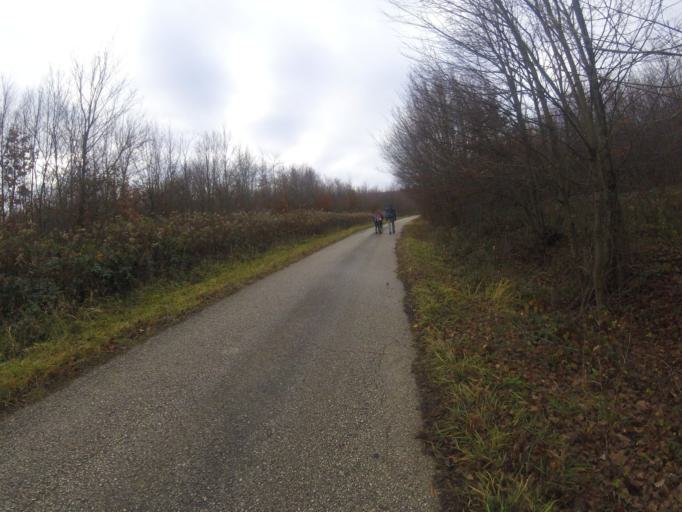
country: HU
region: Veszprem
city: Sumeg
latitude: 46.9091
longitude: 17.3203
